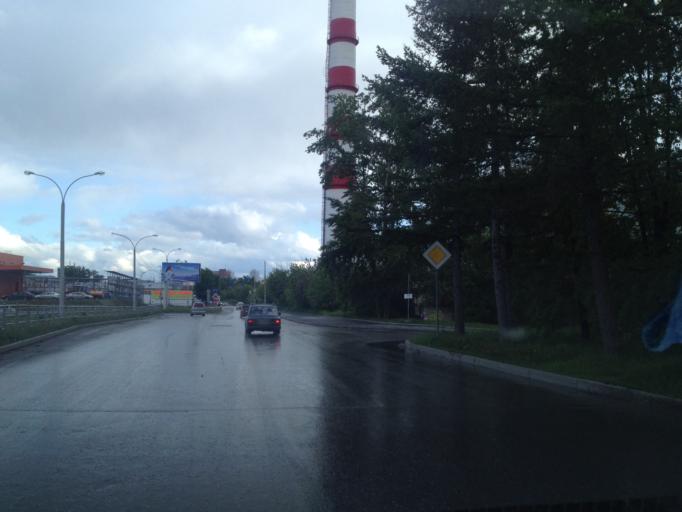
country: RU
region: Sverdlovsk
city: Yekaterinburg
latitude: 56.8517
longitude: 60.5488
